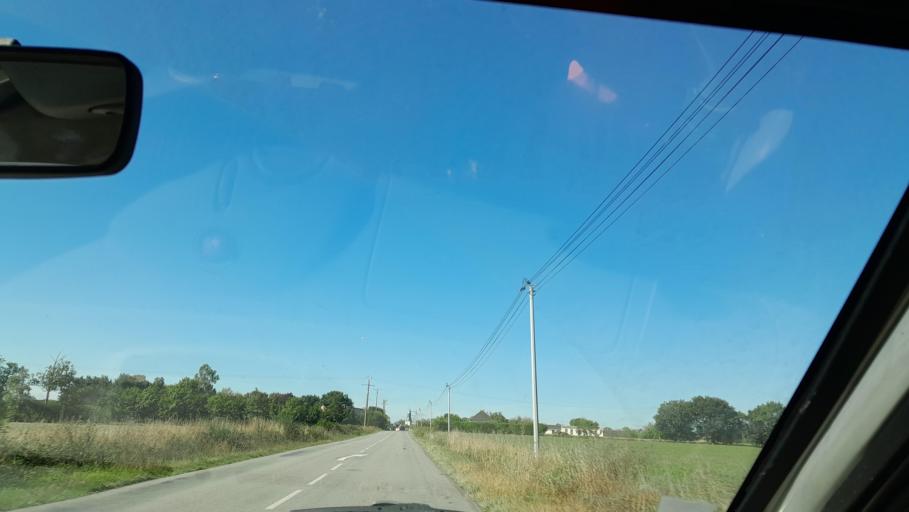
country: FR
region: Pays de la Loire
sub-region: Departement de la Mayenne
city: Ballots
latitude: 47.9452
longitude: -1.0789
